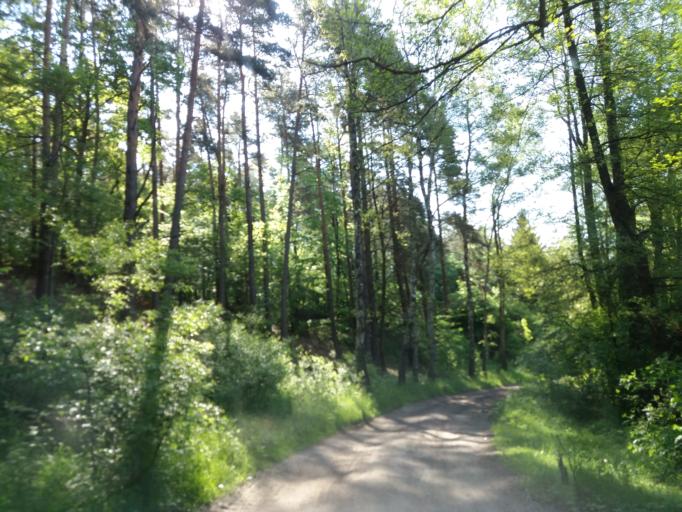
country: PL
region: West Pomeranian Voivodeship
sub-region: Powiat choszczenski
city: Bierzwnik
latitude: 53.0900
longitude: 15.6683
